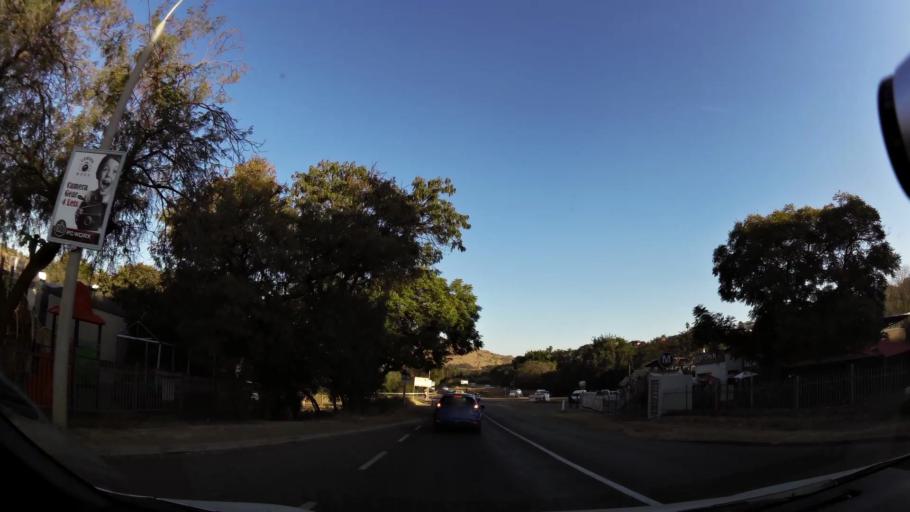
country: ZA
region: North-West
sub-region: Bojanala Platinum District Municipality
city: Rustenburg
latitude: -25.7092
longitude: 27.2399
